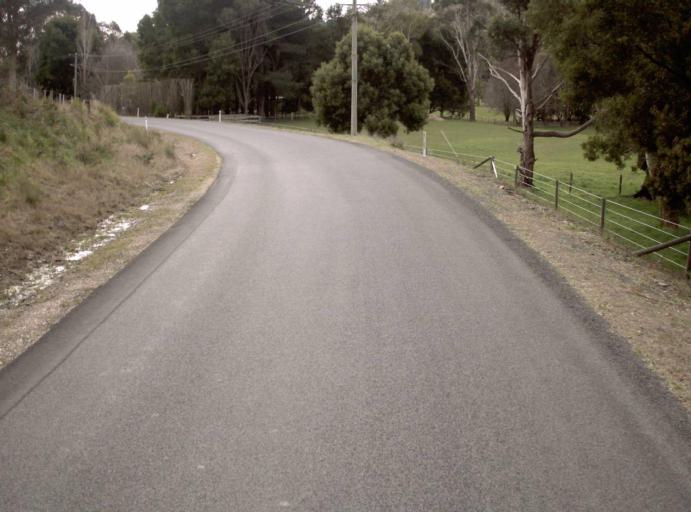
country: AU
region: Tasmania
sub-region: Launceston
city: Mayfield
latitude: -41.2634
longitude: 147.1606
